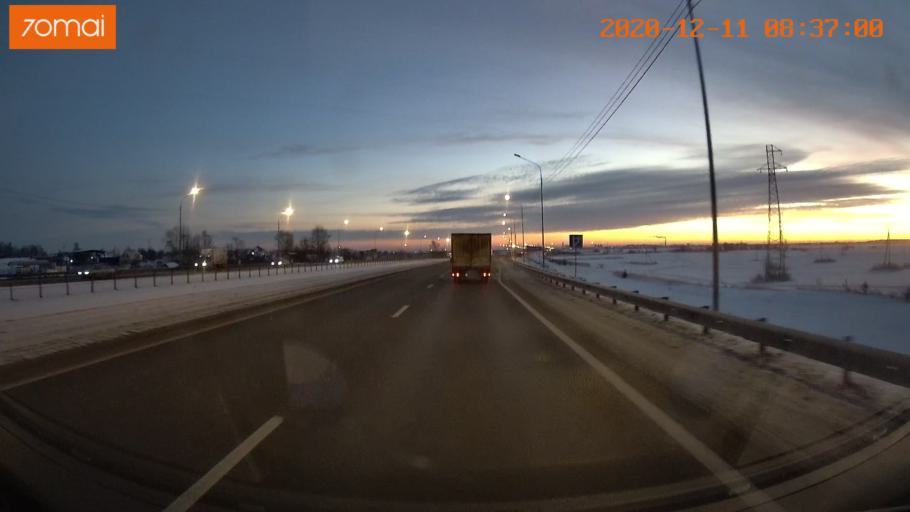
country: RU
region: Vologda
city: Molochnoye
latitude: 59.2092
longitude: 39.6941
